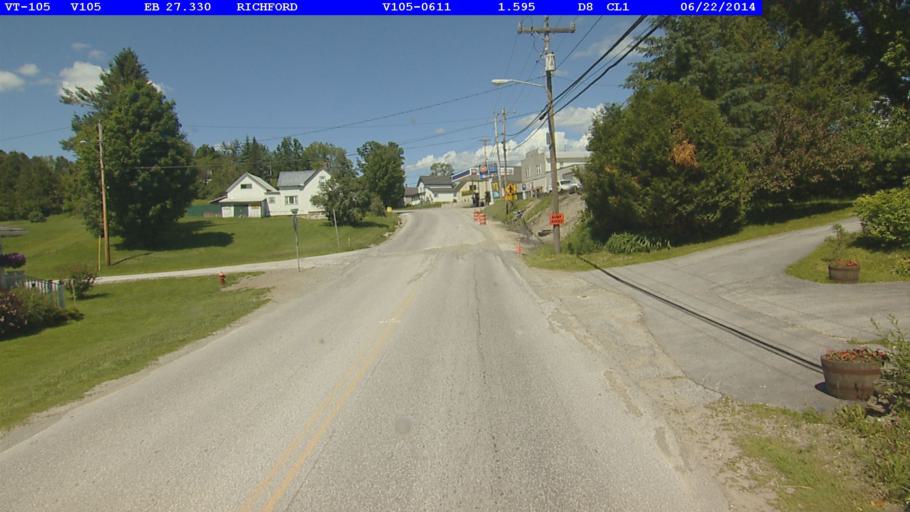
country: US
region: Vermont
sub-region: Franklin County
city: Richford
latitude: 44.9893
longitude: -72.6763
